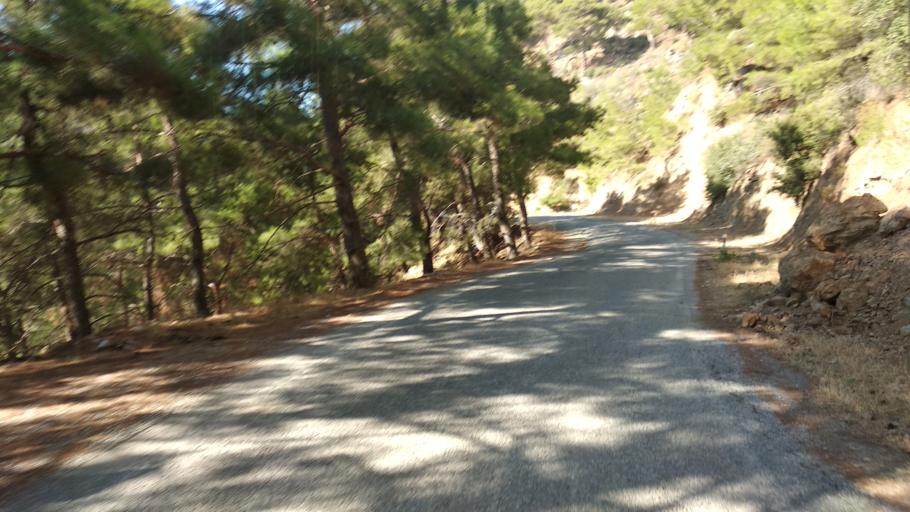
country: TR
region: Izmir
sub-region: Seferihisar
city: Seferhisar
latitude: 38.3179
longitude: 26.9580
